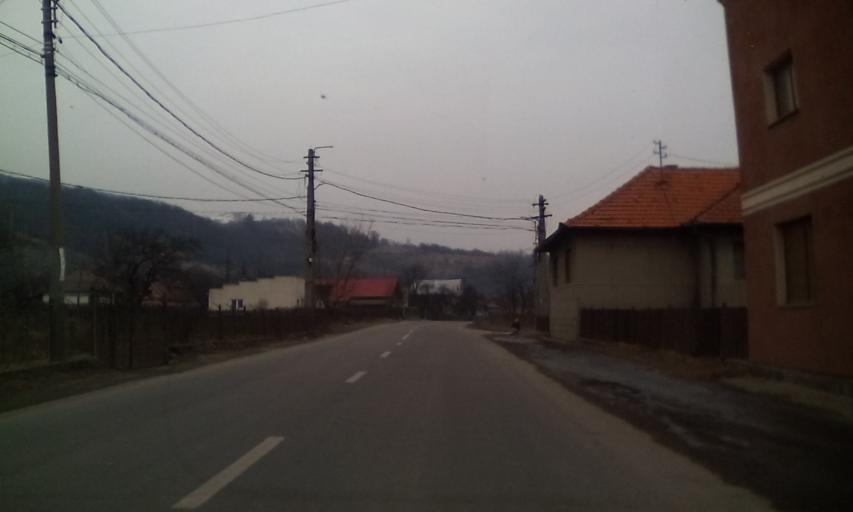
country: RO
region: Hunedoara
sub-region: Comuna Uricani
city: Uricani
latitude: 45.3354
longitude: 23.1321
